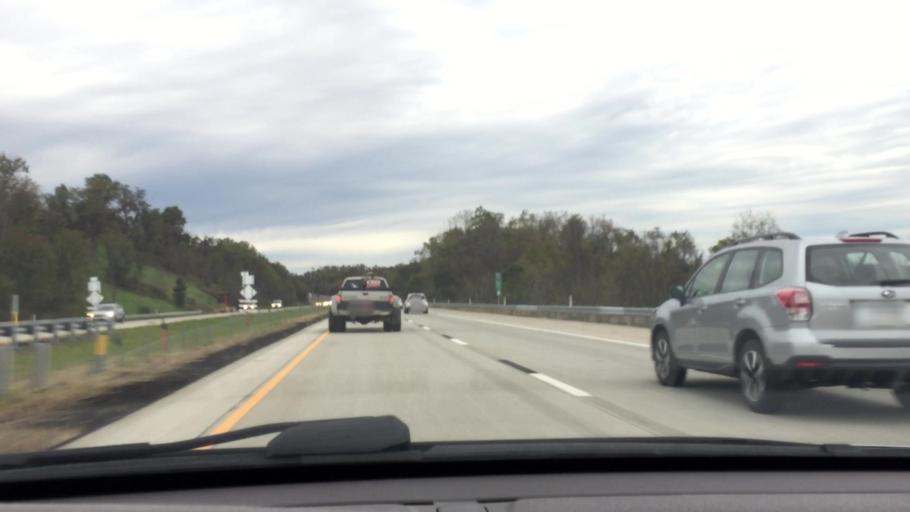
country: US
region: Pennsylvania
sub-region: Allegheny County
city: Carnot-Moon
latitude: 40.5360
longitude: -80.2722
